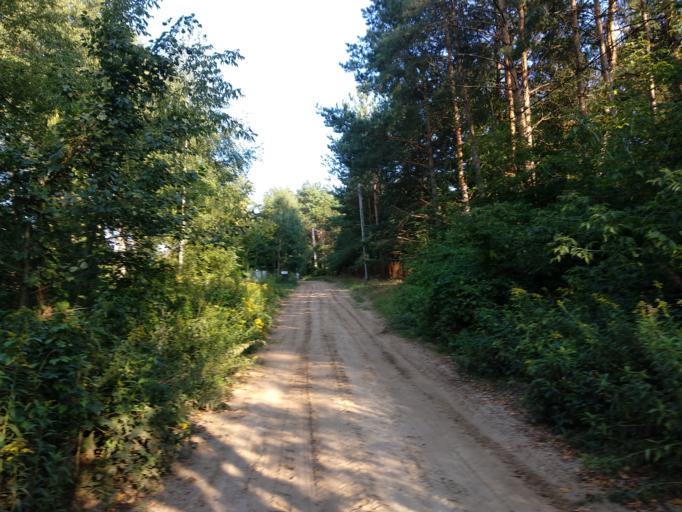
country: PL
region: Masovian Voivodeship
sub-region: Powiat pultuski
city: Obryte
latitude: 52.7571
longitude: 21.1857
